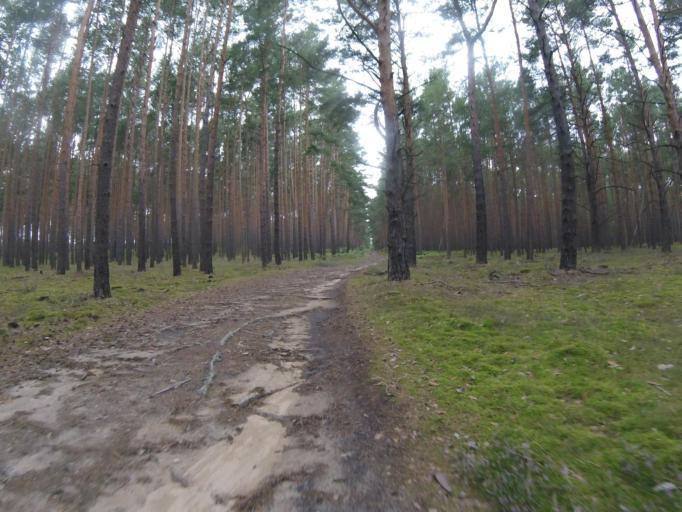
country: DE
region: Brandenburg
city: Gross Koris
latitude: 52.2069
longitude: 13.6620
